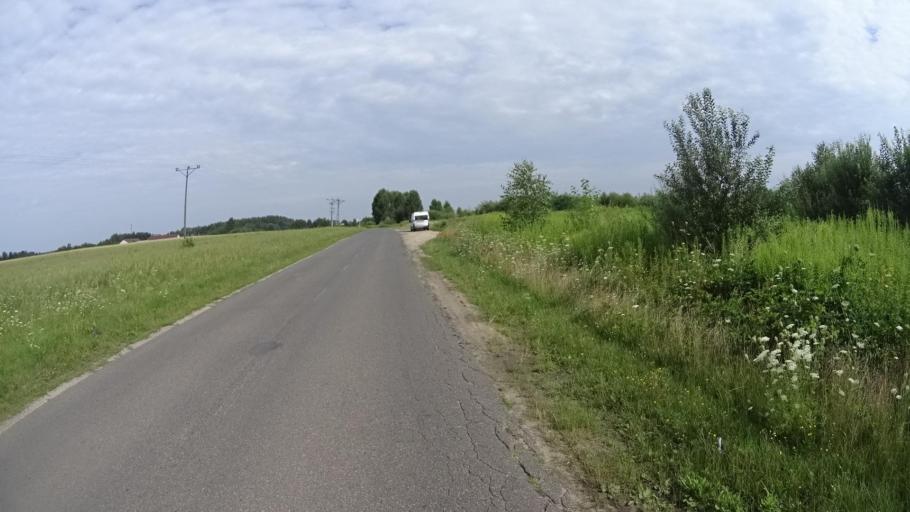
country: PL
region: Masovian Voivodeship
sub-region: Powiat piaseczynski
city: Tarczyn
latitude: 52.0126
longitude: 20.8018
